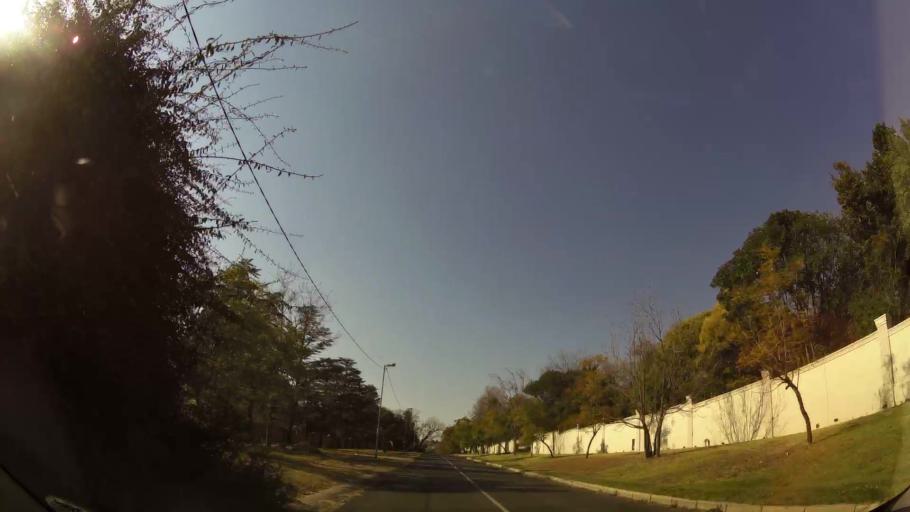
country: ZA
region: Gauteng
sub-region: City of Johannesburg Metropolitan Municipality
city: Diepsloot
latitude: -26.0644
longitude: 28.0104
